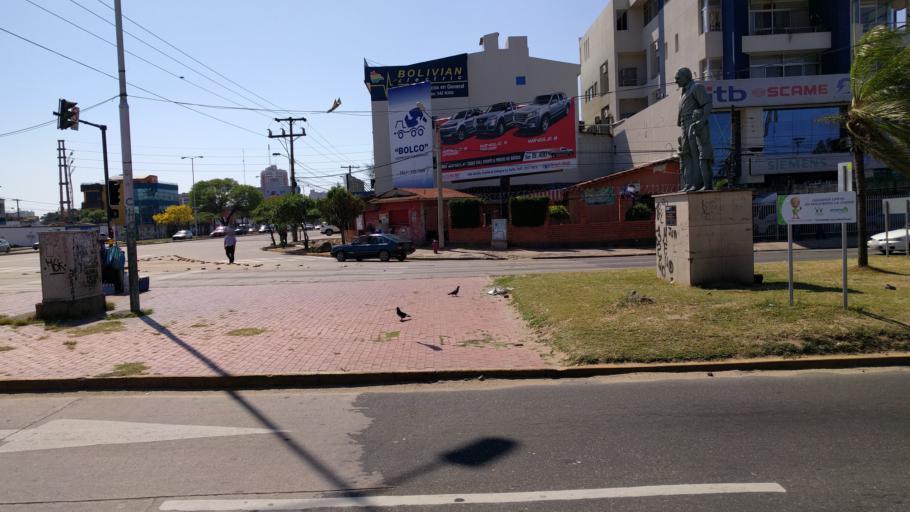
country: BO
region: Santa Cruz
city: Santa Cruz de la Sierra
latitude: -17.7823
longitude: -63.1644
